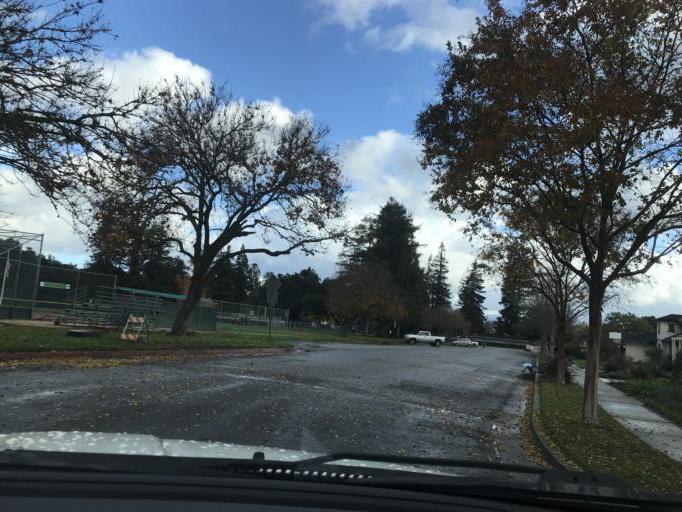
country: US
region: California
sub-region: Santa Clara County
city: Buena Vista
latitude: 37.3023
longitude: -121.9100
